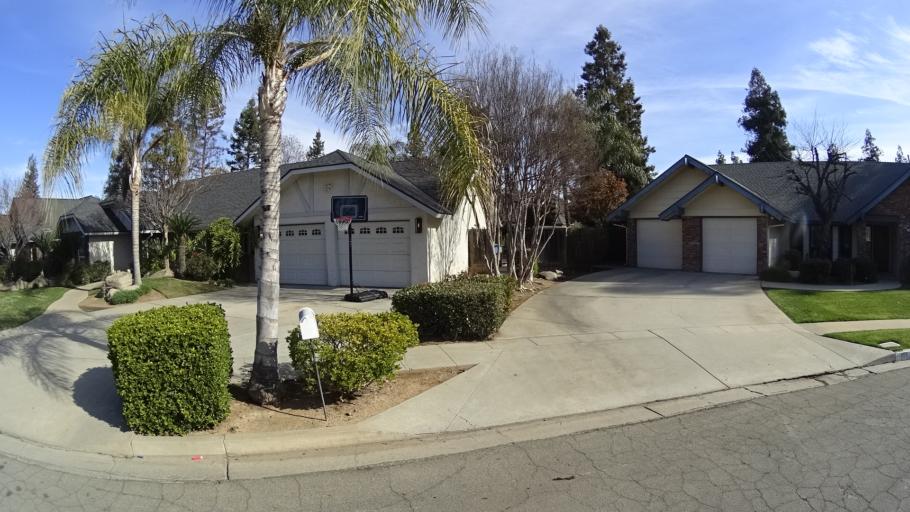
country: US
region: California
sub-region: Fresno County
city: Clovis
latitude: 36.8616
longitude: -119.7770
